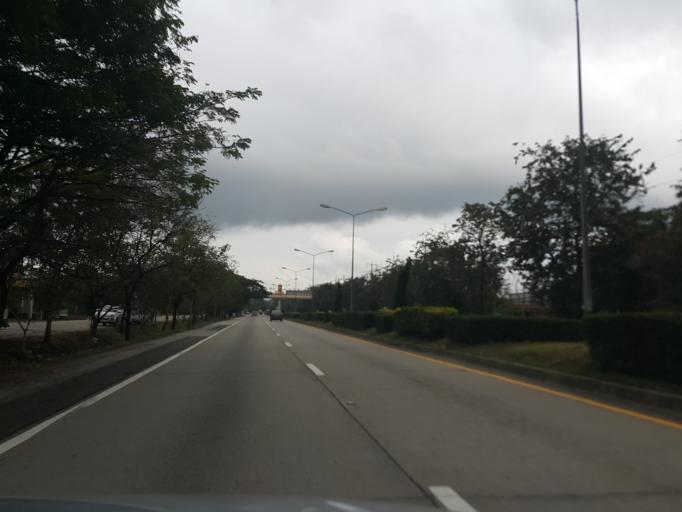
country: TH
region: Lampang
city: Lampang
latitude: 18.2746
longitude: 99.4579
